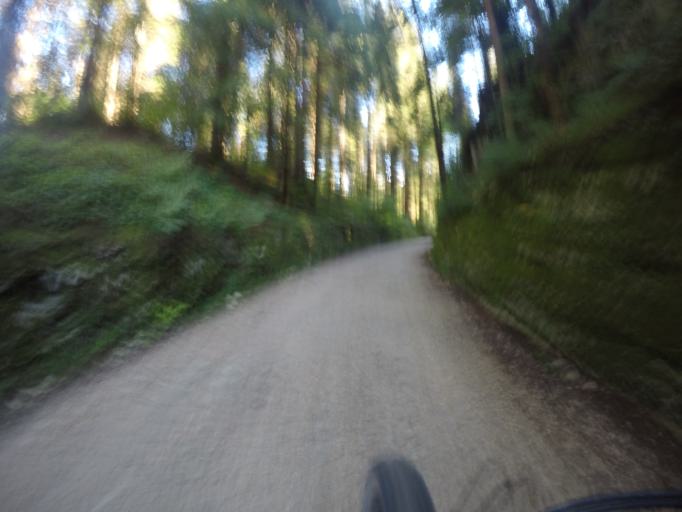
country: IT
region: Veneto
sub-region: Provincia di Vicenza
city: Canove di Roana
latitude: 45.8493
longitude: 11.4738
